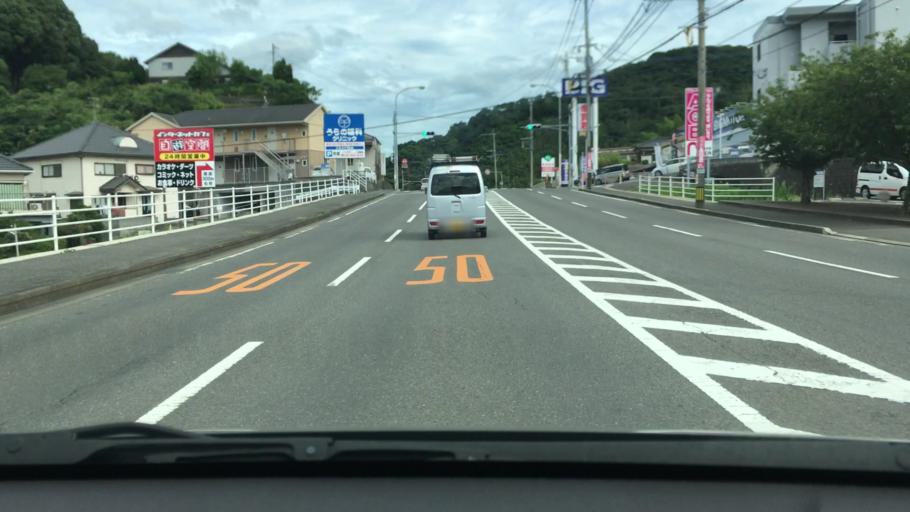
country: JP
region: Nagasaki
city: Togitsu
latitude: 32.8356
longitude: 129.8390
